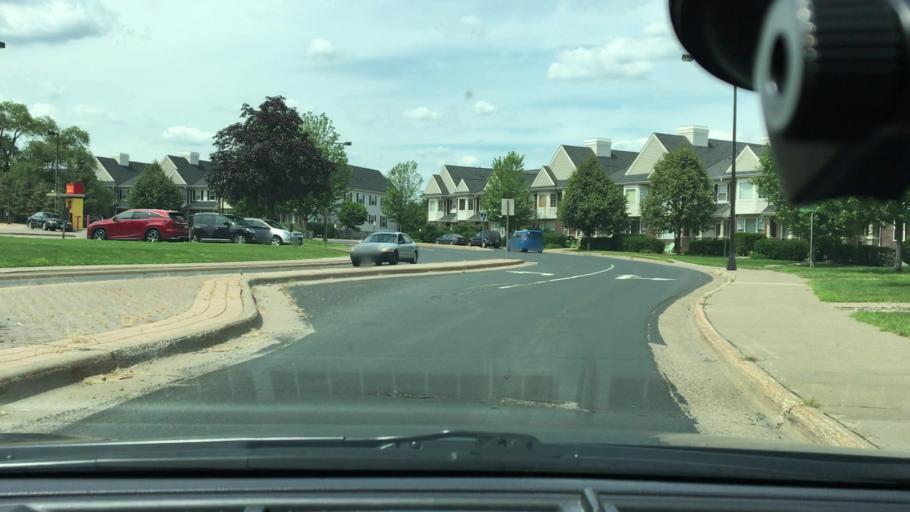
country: US
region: Minnesota
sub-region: Hennepin County
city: Golden Valley
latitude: 44.9860
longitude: -93.3835
